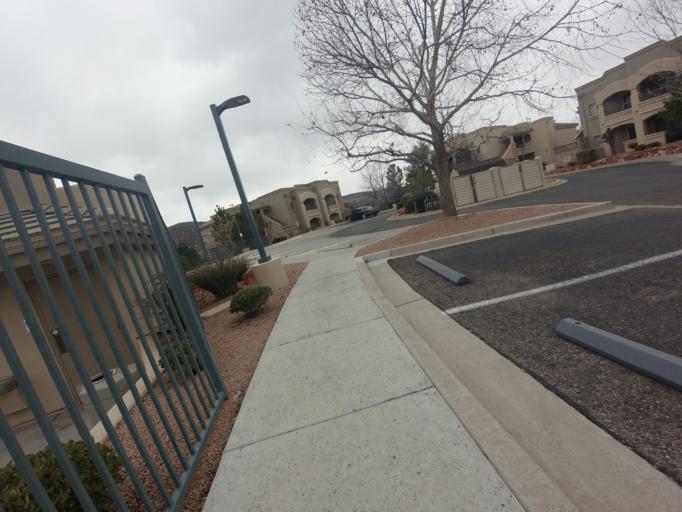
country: US
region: Arizona
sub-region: Yavapai County
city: Big Park
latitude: 34.7722
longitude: -111.7694
